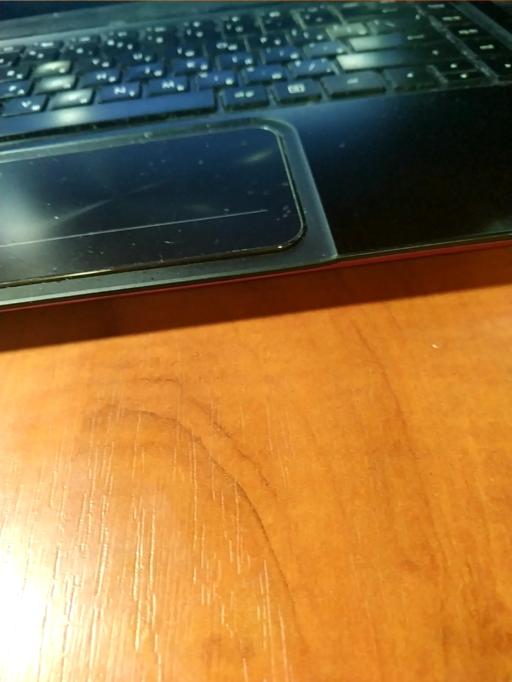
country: RU
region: Tverskaya
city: Likhoslavl'
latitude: 57.2199
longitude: 35.3662
